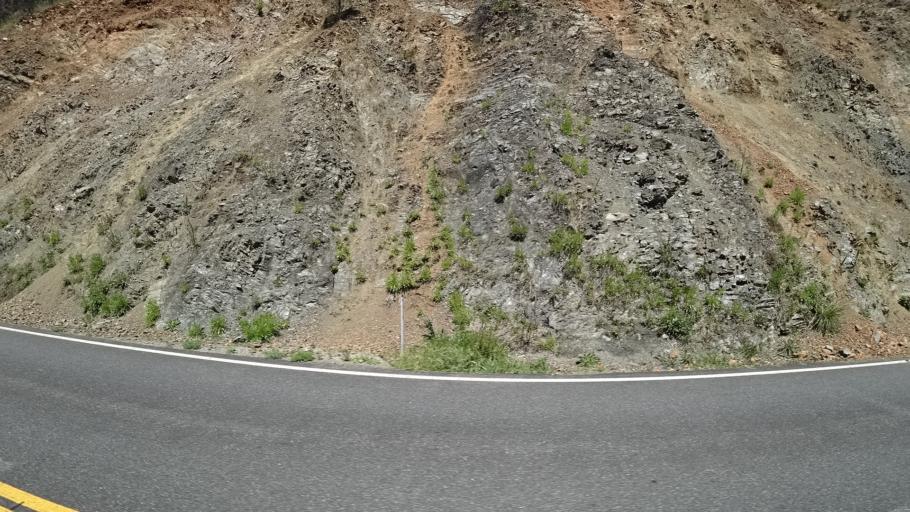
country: US
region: California
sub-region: Trinity County
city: Weaverville
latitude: 40.7615
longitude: -123.0693
